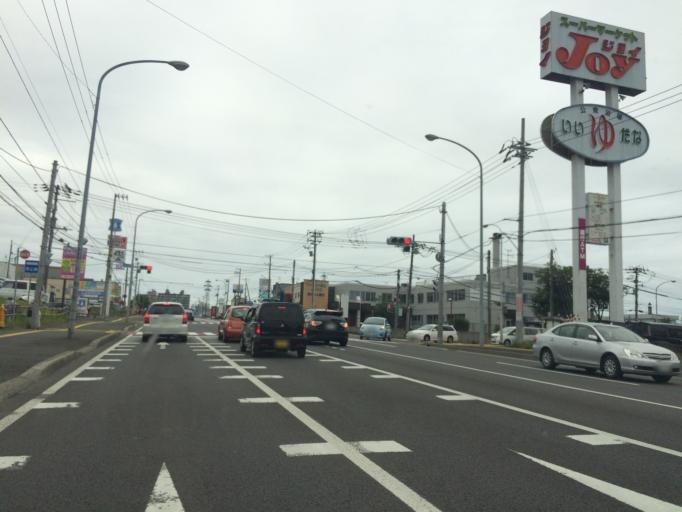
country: JP
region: Hokkaido
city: Sapporo
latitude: 43.1276
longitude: 141.2151
